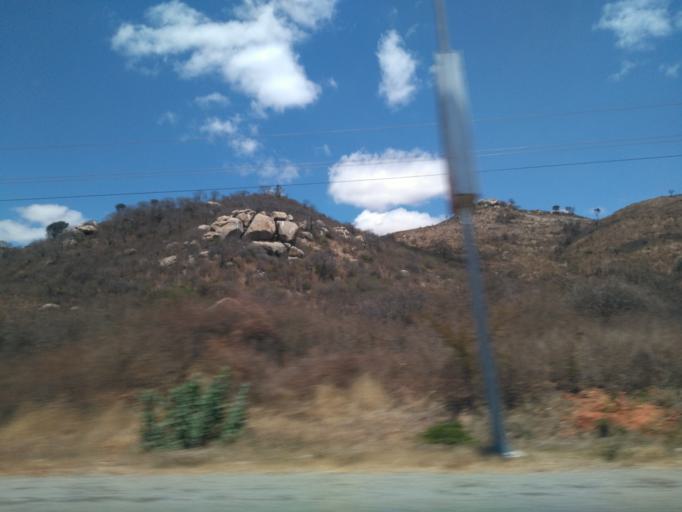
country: TZ
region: Dodoma
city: Kisasa
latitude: -6.2195
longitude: 35.7856
